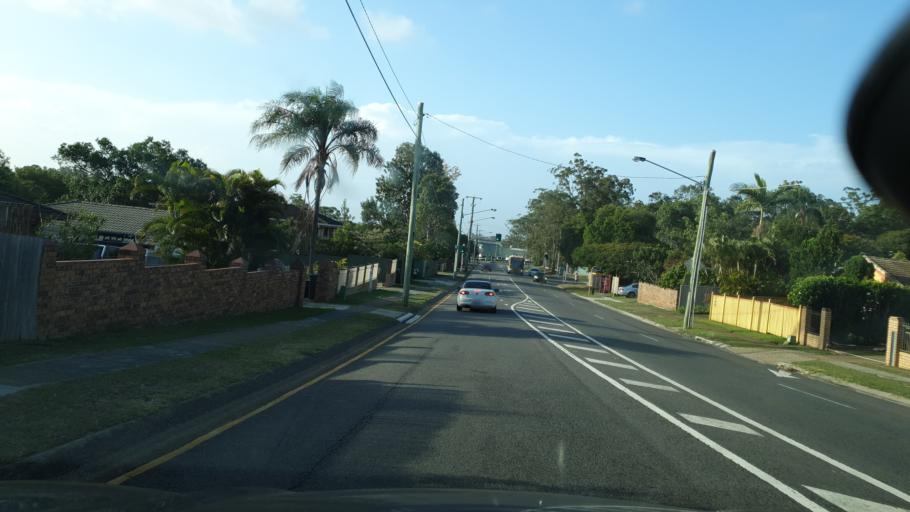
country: AU
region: Queensland
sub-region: Brisbane
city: Belmont
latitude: -27.4873
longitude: 153.1269
